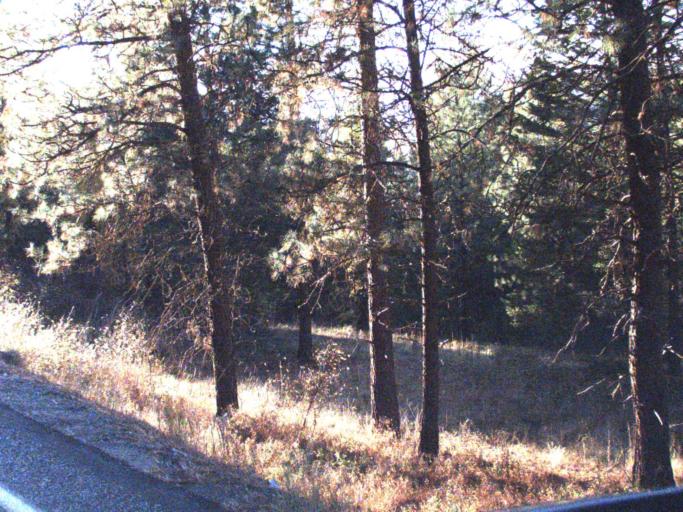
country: CA
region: British Columbia
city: Rossland
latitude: 48.8656
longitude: -117.8703
